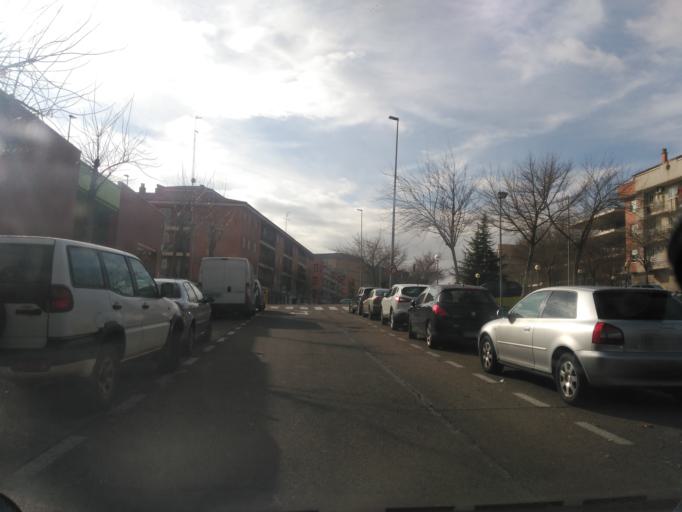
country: ES
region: Castille and Leon
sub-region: Provincia de Salamanca
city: Salamanca
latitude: 40.9620
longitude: -5.6499
